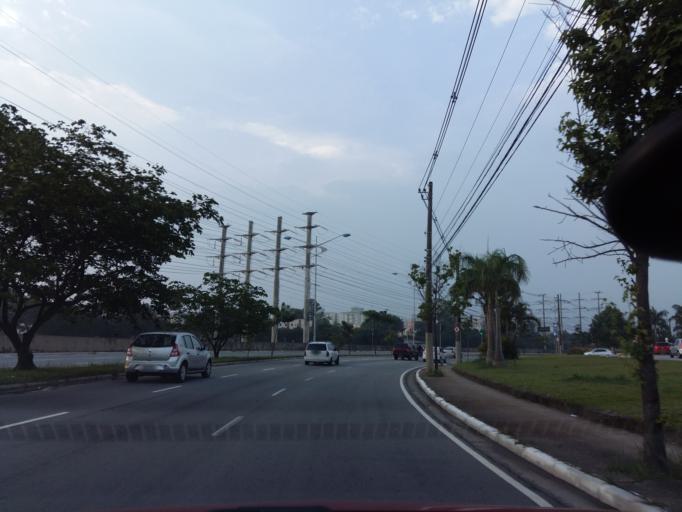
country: BR
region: Sao Paulo
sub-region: Sao Caetano Do Sul
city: Sao Caetano do Sul
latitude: -23.6268
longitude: -46.5822
